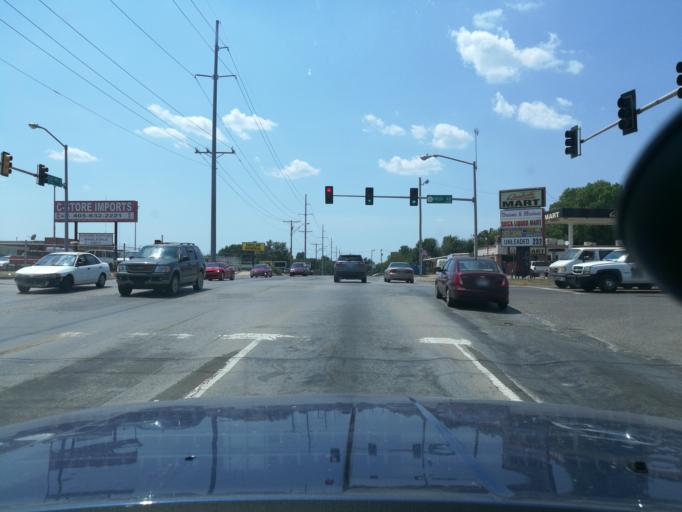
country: US
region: Oklahoma
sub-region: Oklahoma County
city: Oklahoma City
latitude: 35.4208
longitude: -97.4946
